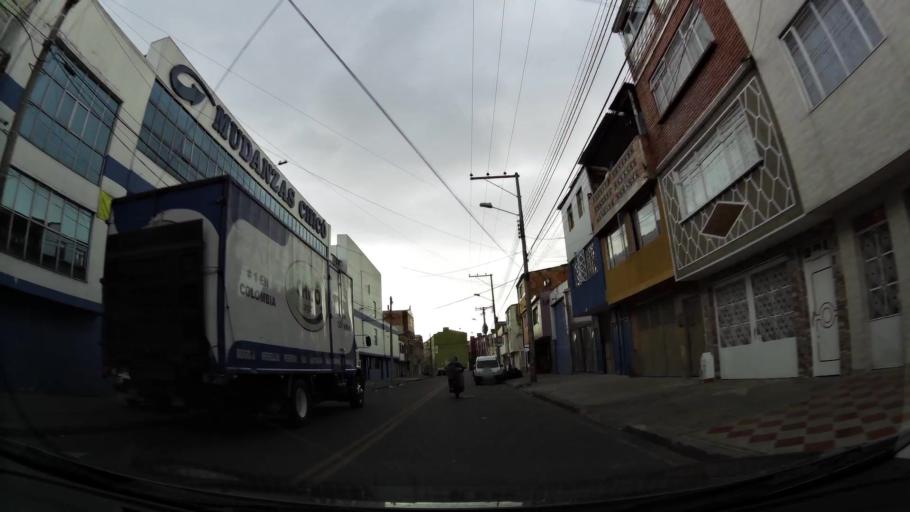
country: CO
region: Bogota D.C.
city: Barrio San Luis
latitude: 4.6735
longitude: -74.0747
